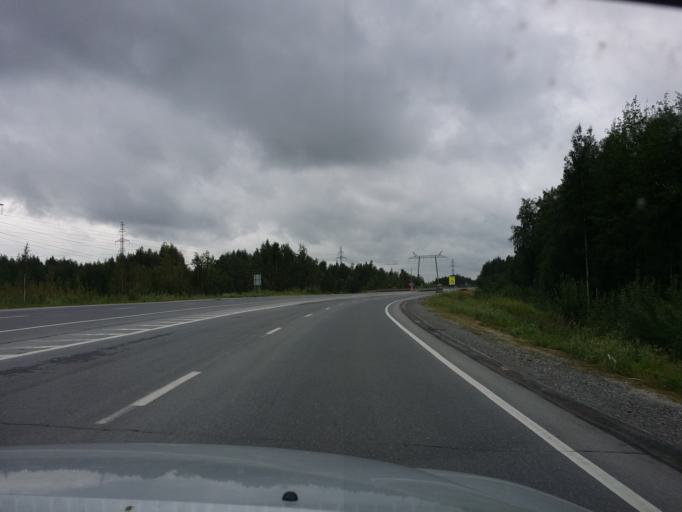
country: RU
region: Khanty-Mansiyskiy Avtonomnyy Okrug
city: Megion
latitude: 61.0497
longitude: 76.3382
